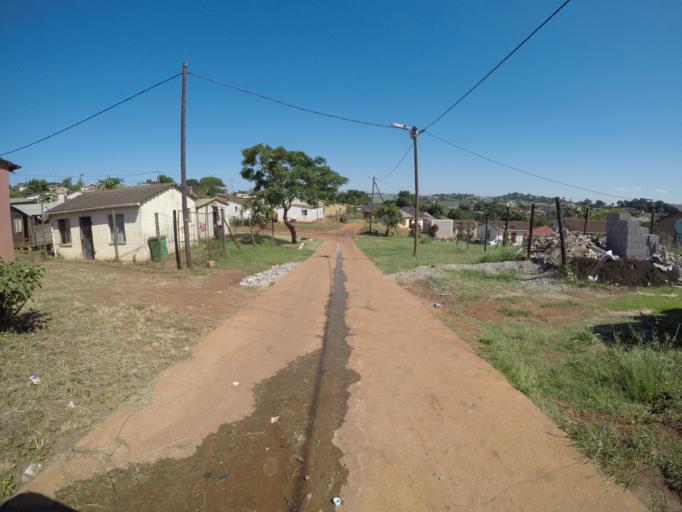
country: ZA
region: KwaZulu-Natal
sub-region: uThungulu District Municipality
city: Empangeni
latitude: -28.7738
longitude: 31.8765
